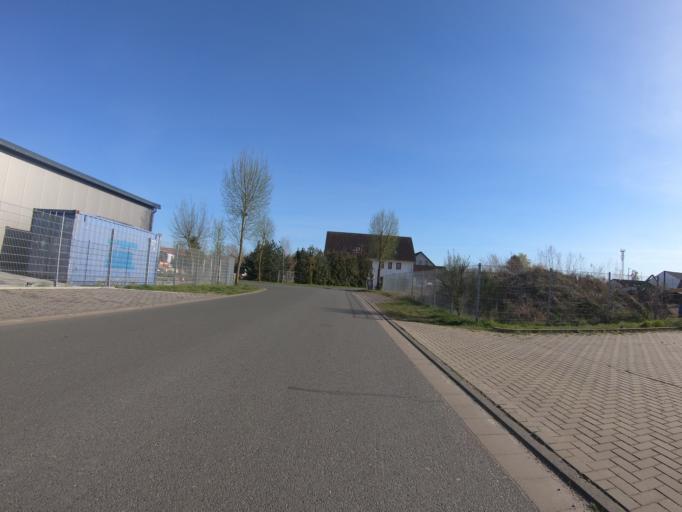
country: DE
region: Lower Saxony
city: Isenbuttel
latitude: 52.4488
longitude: 10.5821
